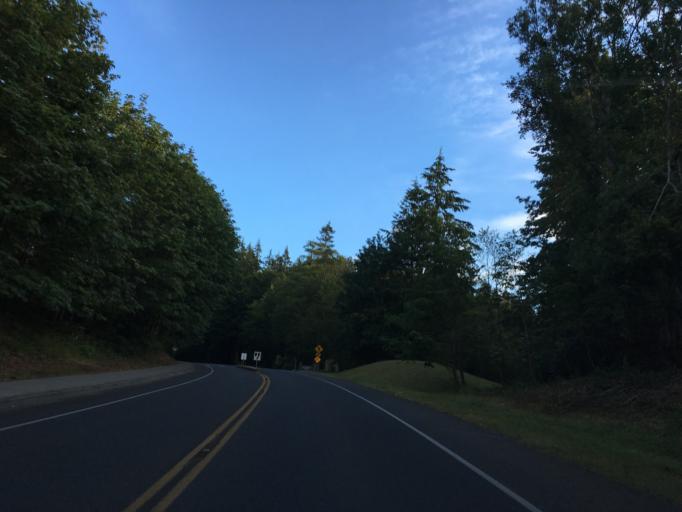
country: CA
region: British Columbia
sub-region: Greater Vancouver Regional District
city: White Rock
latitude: 48.9751
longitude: -122.7924
